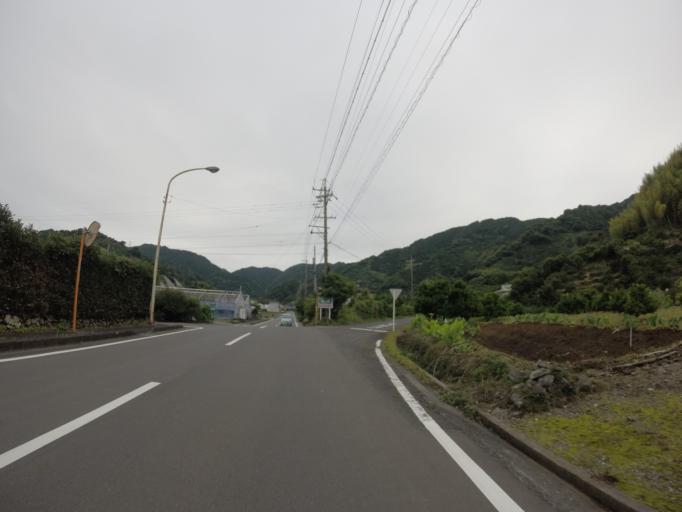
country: JP
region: Shizuoka
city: Shizuoka-shi
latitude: 34.9289
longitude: 138.3541
